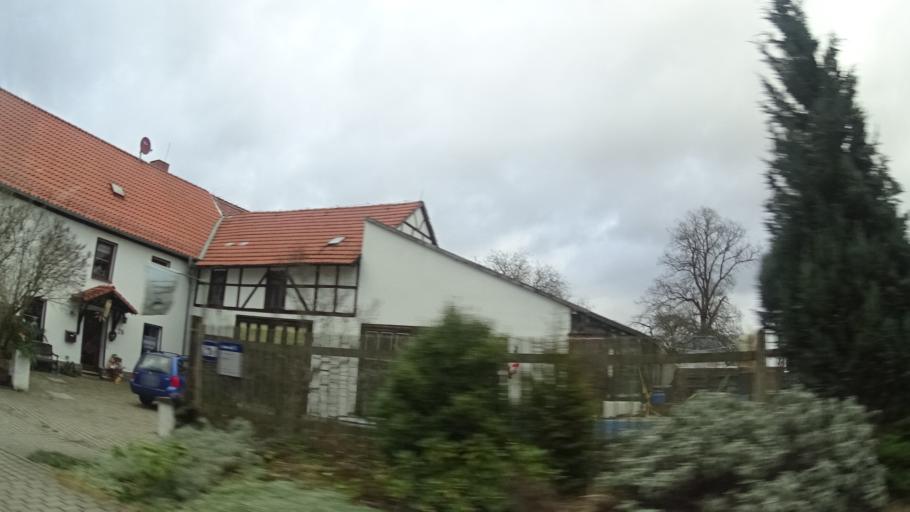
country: DE
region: Thuringia
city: Lemnitz
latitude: 50.7172
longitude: 11.8459
